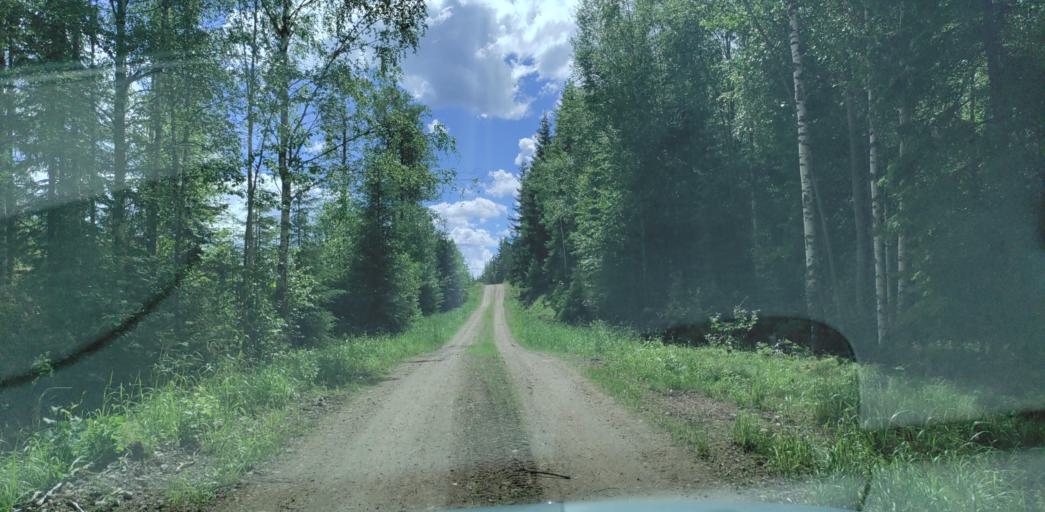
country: SE
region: Vaermland
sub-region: Hagfors Kommun
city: Ekshaerad
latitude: 60.1164
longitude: 13.3260
